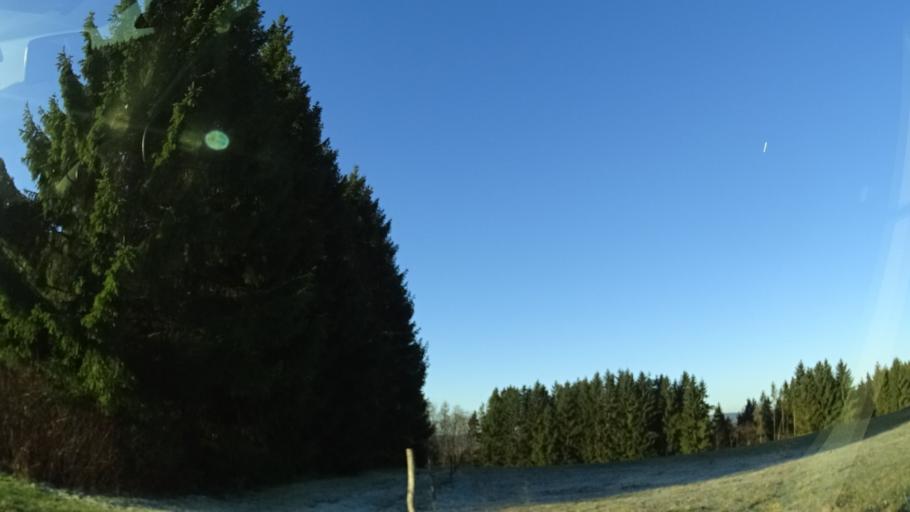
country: DE
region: Thuringia
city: Judenbach
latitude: 50.4337
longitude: 11.2393
